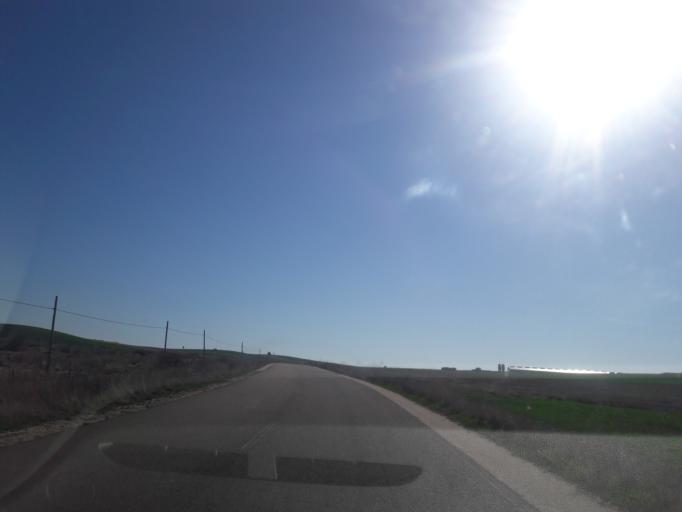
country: ES
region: Castille and Leon
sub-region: Provincia de Salamanca
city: Tordillos
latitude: 40.8511
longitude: -5.3393
